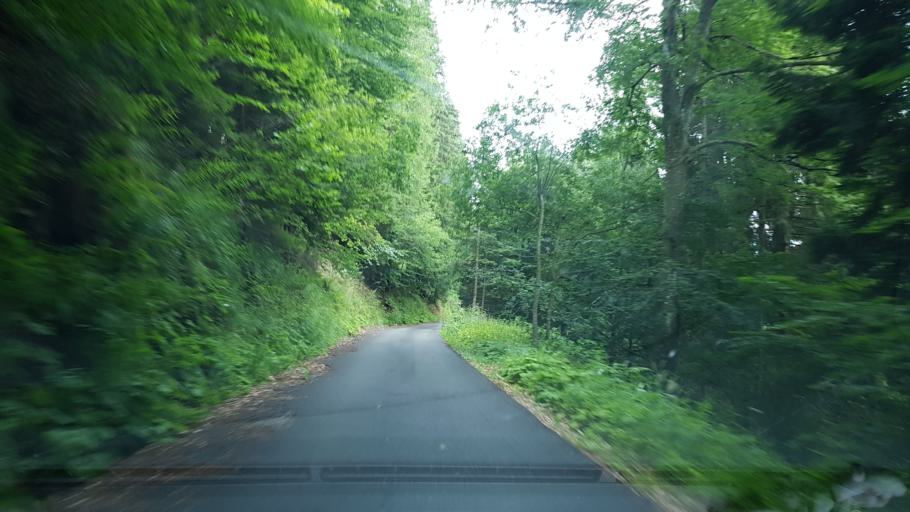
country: IT
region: Friuli Venezia Giulia
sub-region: Provincia di Udine
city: Cercivento
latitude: 46.5423
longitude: 12.9863
